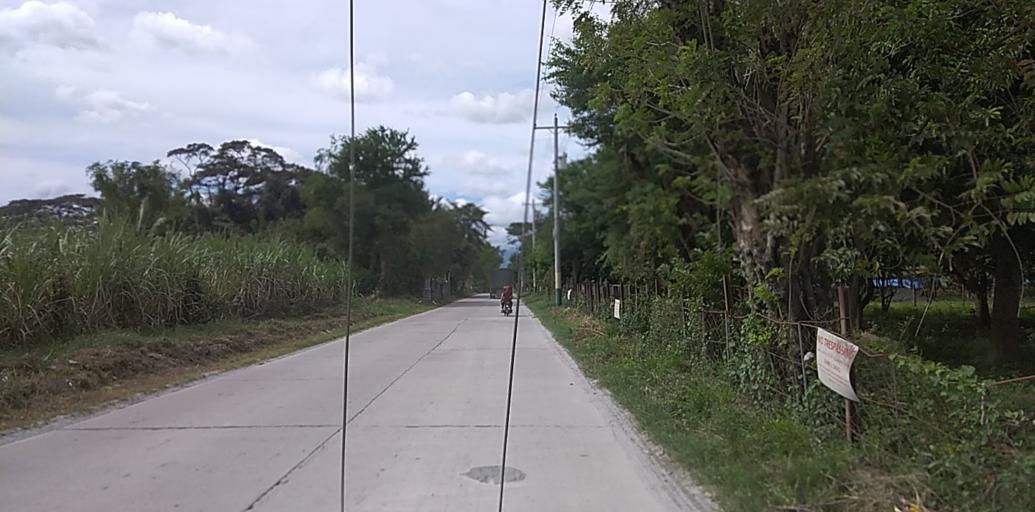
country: PH
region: Central Luzon
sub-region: Province of Pampanga
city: Pulung Santol
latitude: 15.0672
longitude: 120.5645
